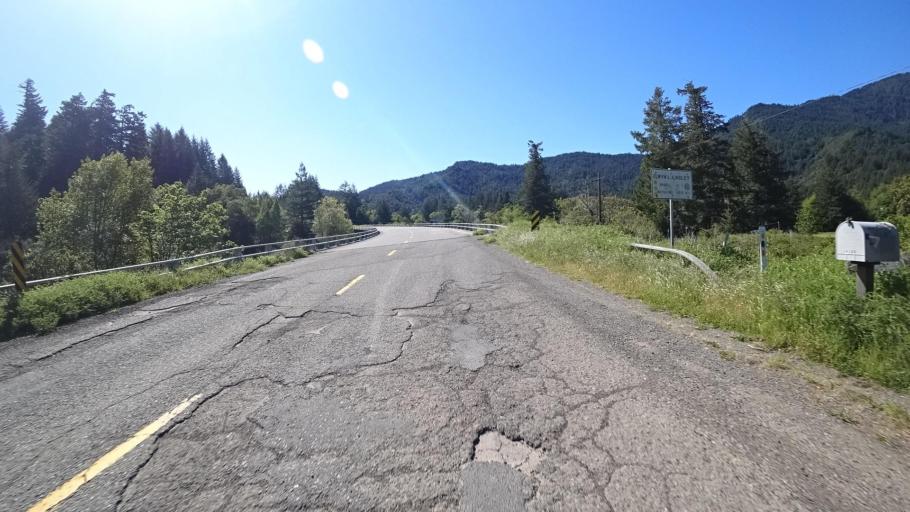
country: US
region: California
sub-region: Humboldt County
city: Rio Dell
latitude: 40.2772
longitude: -124.2431
